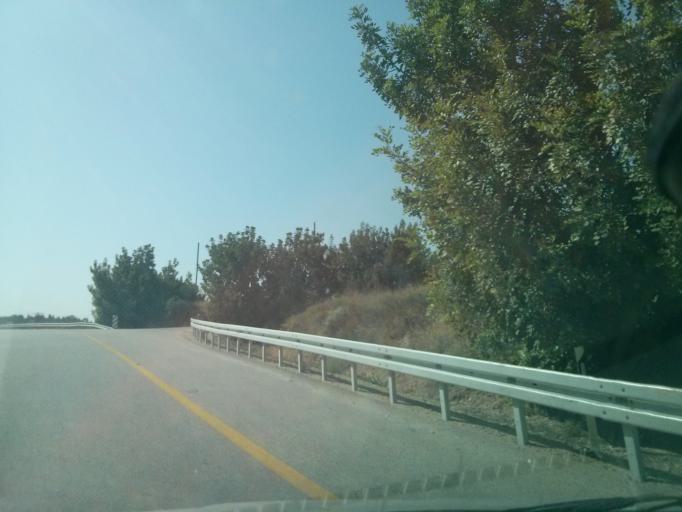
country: PS
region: West Bank
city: Surif
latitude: 31.6737
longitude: 35.0116
